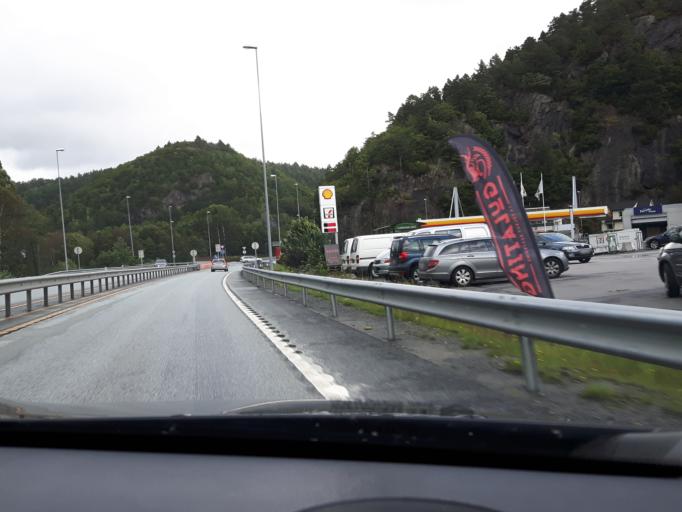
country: NO
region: Vest-Agder
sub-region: Songdalen
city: Nodeland
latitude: 58.1347
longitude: 7.8555
